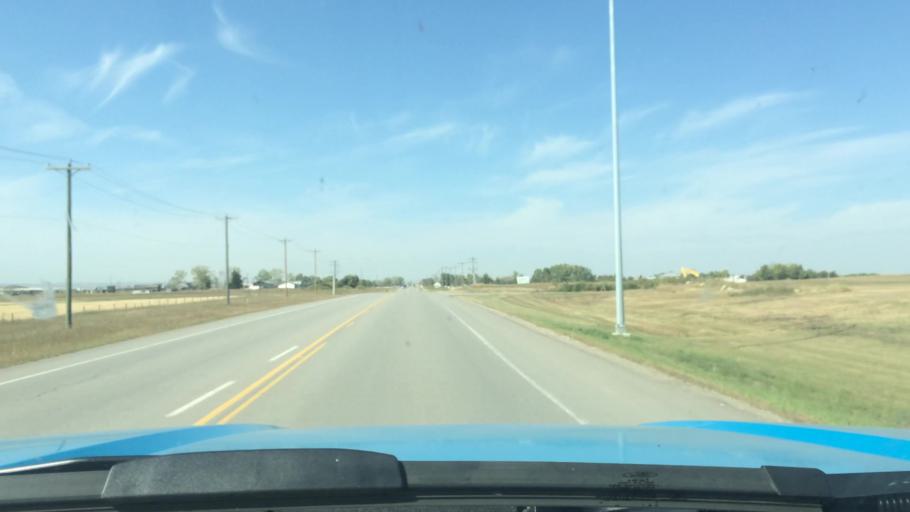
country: CA
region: Alberta
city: Airdrie
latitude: 51.2133
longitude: -113.9400
